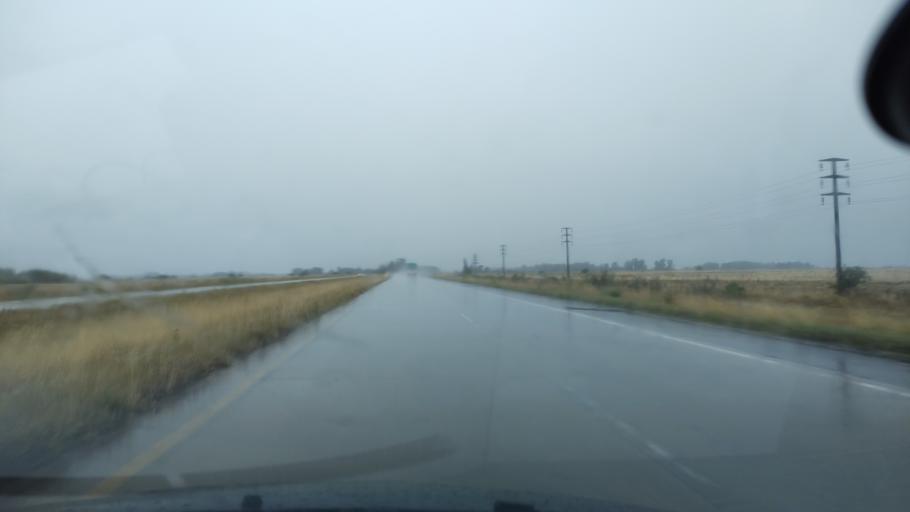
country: AR
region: Buenos Aires
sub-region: Partido de San Vicente
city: San Vicente
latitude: -35.0710
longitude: -58.5278
